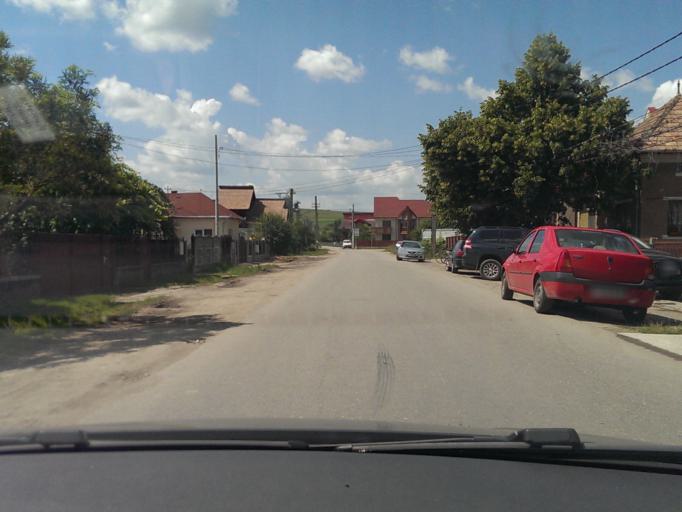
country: RO
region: Cluj
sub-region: Comuna Apahida
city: Sannicoara
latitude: 46.7914
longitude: 23.7242
